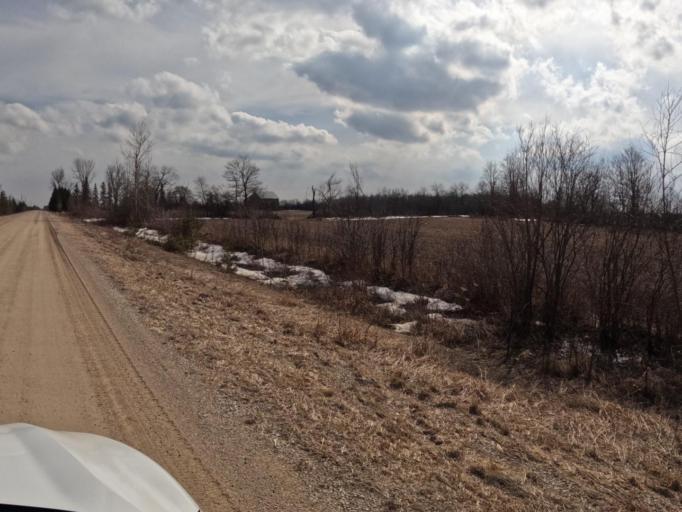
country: CA
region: Ontario
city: Shelburne
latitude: 43.9369
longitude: -80.3099
